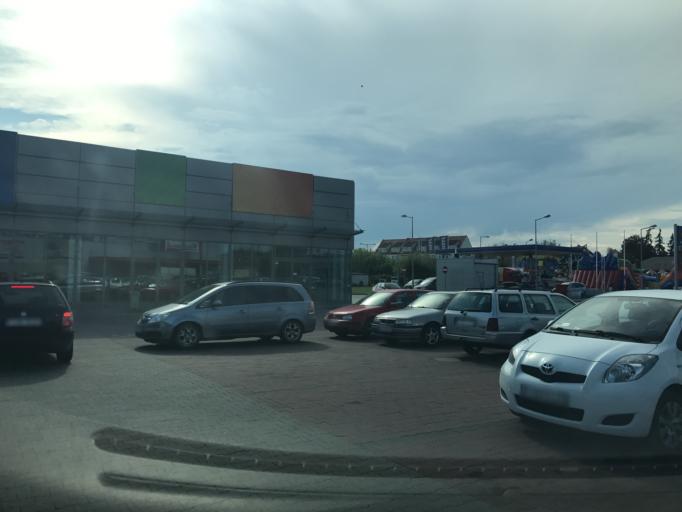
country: PL
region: Kujawsko-Pomorskie
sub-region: Powiat swiecki
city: Swiecie
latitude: 53.4064
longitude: 18.4394
